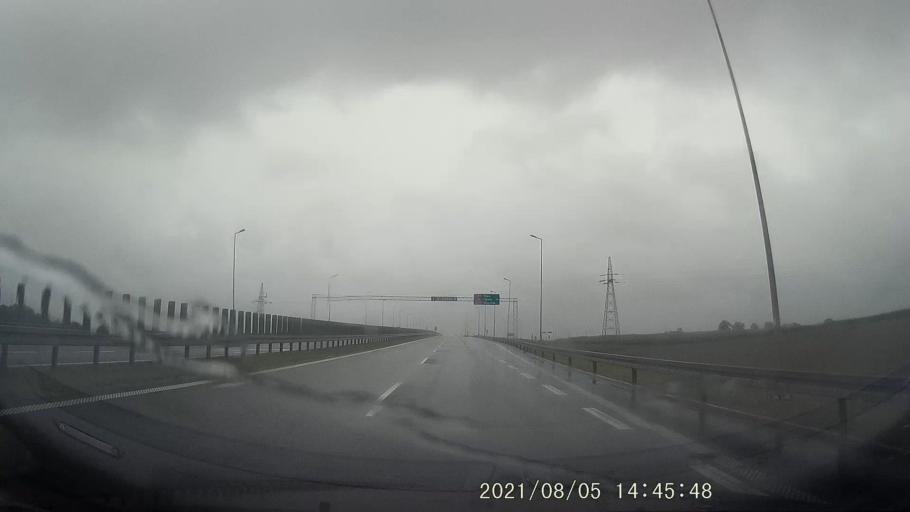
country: PL
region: Opole Voivodeship
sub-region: Powiat nyski
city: Nysa
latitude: 50.5001
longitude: 17.3518
